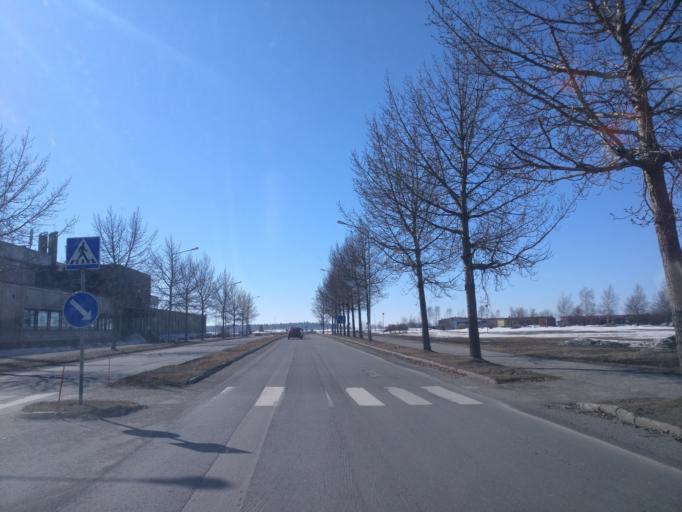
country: FI
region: Lapland
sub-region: Kemi-Tornio
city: Kemi
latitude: 65.7377
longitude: 24.5565
